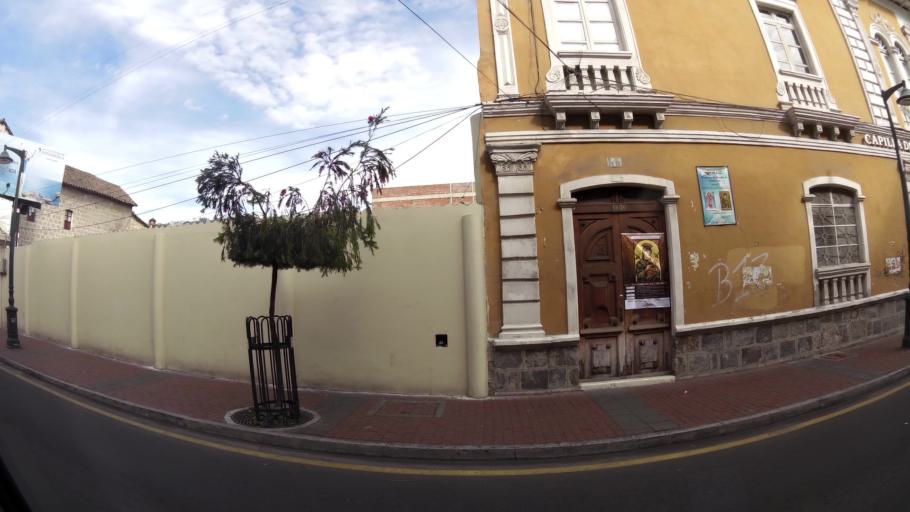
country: EC
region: Tungurahua
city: Ambato
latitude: -1.2423
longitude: -78.6259
